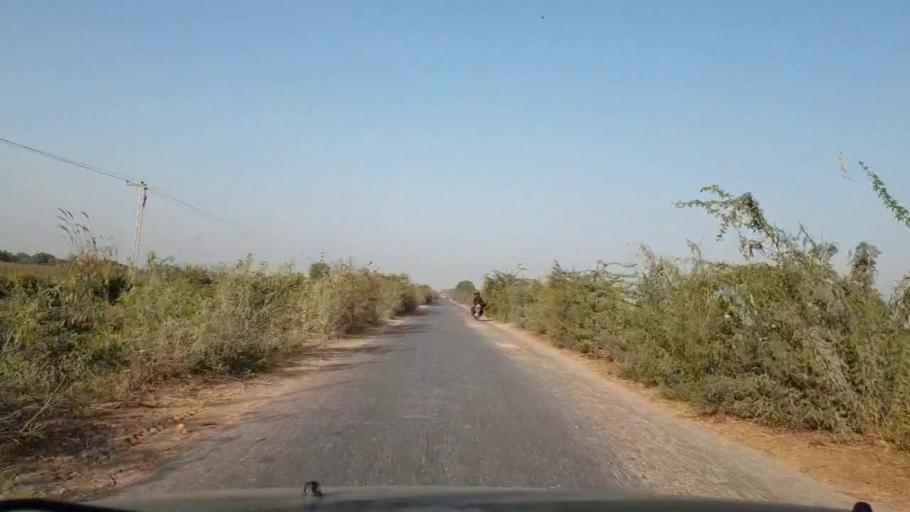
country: PK
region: Sindh
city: Chambar
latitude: 25.2721
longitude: 68.8039
